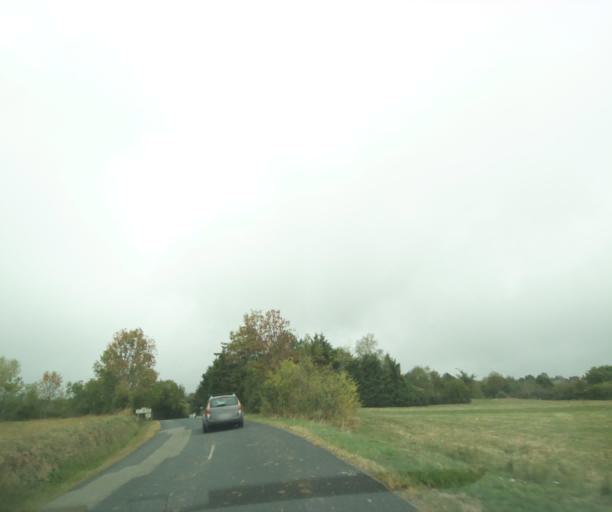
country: FR
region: Auvergne
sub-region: Departement du Puy-de-Dome
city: Saint-Genes-Champanelle
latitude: 45.7222
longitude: 3.0364
